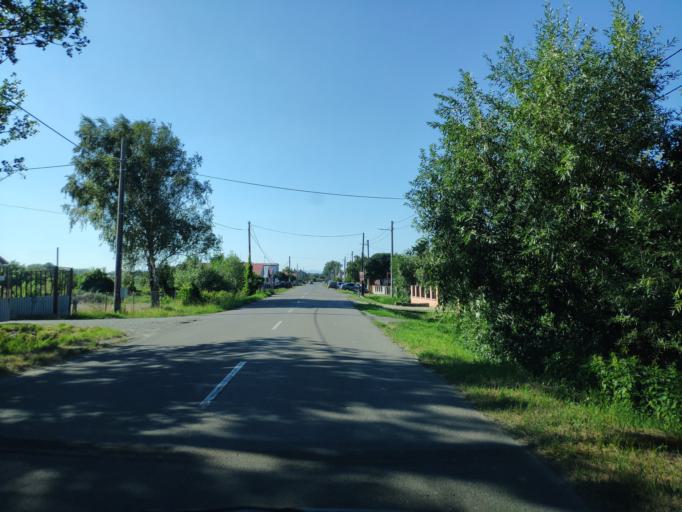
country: SK
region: Kosicky
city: Trebisov
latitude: 48.5698
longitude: 21.8598
